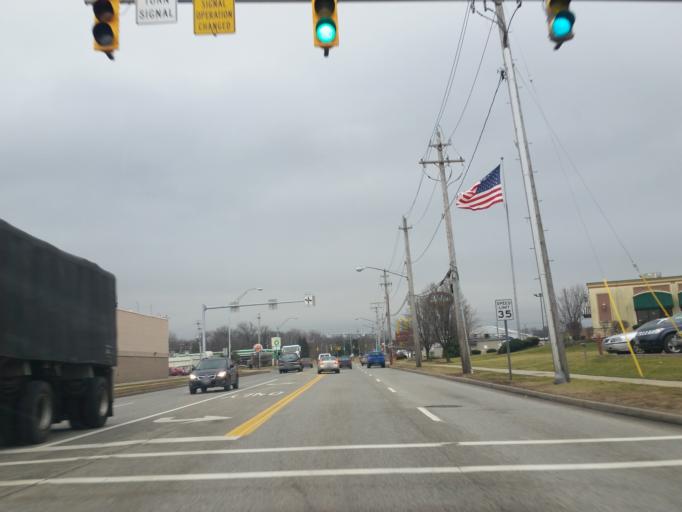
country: US
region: Ohio
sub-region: Cuyahoga County
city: Brooklyn
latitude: 41.4206
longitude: -81.7588
